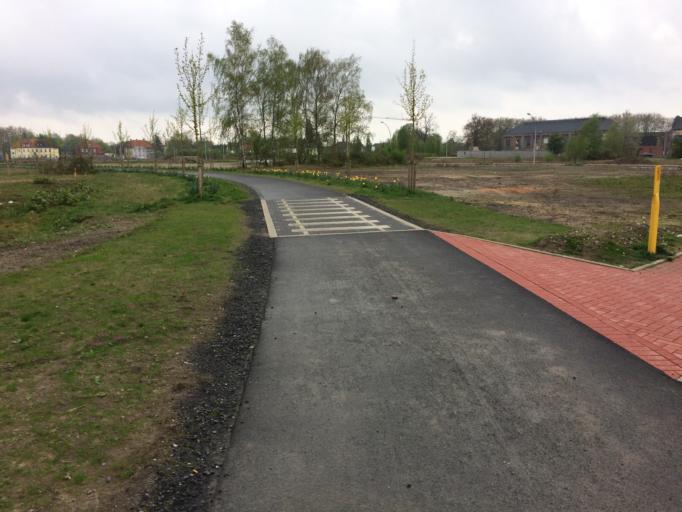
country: DE
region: North Rhine-Westphalia
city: Dorsten
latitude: 51.6745
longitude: 6.9872
